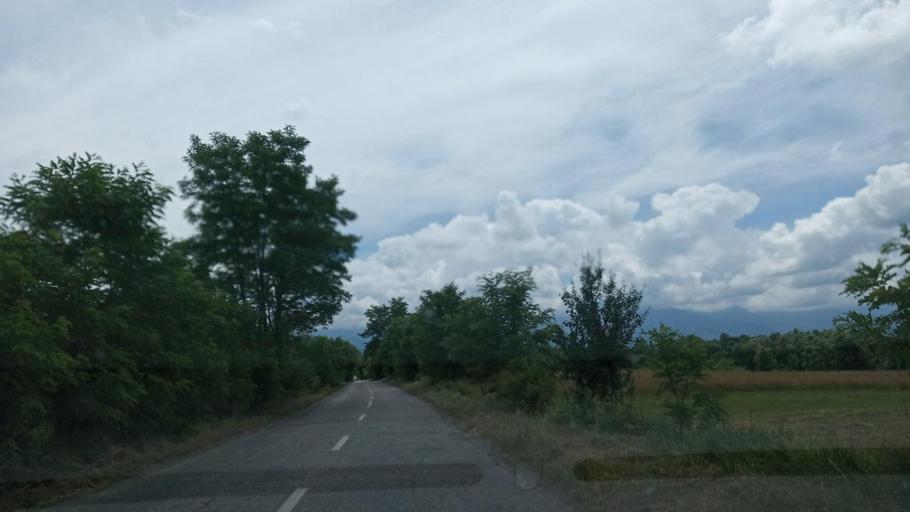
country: RO
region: Sibiu
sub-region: Comuna Porumbacu de Jos
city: Porumbacu de Jos
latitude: 45.7375
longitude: 24.4664
